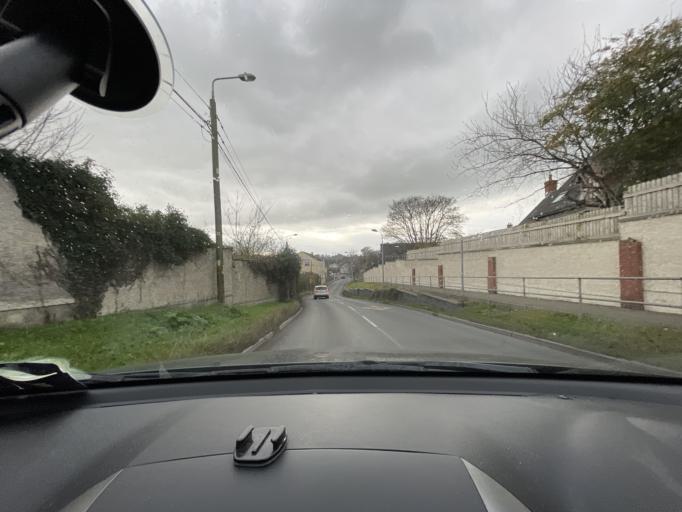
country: IE
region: Leinster
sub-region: Lu
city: Drogheda
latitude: 53.7200
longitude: -6.3290
